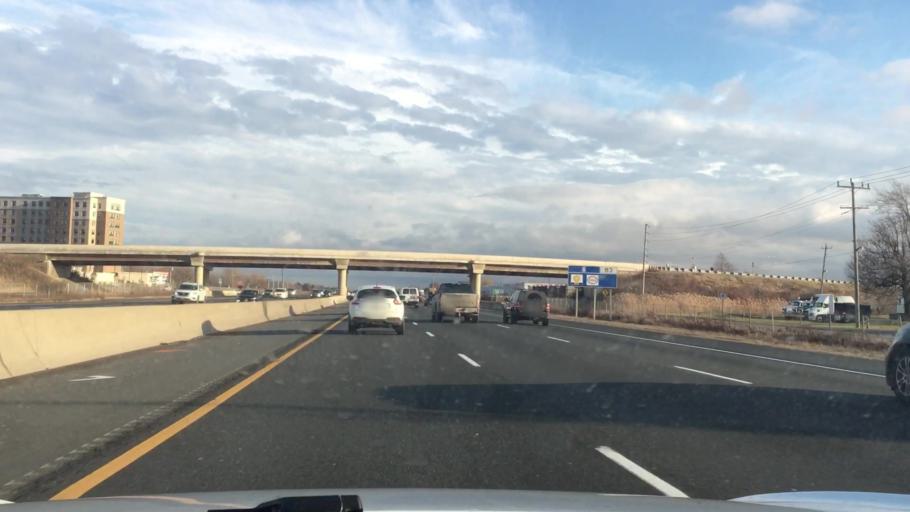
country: CA
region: Ontario
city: Hamilton
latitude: 43.2369
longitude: -79.7208
